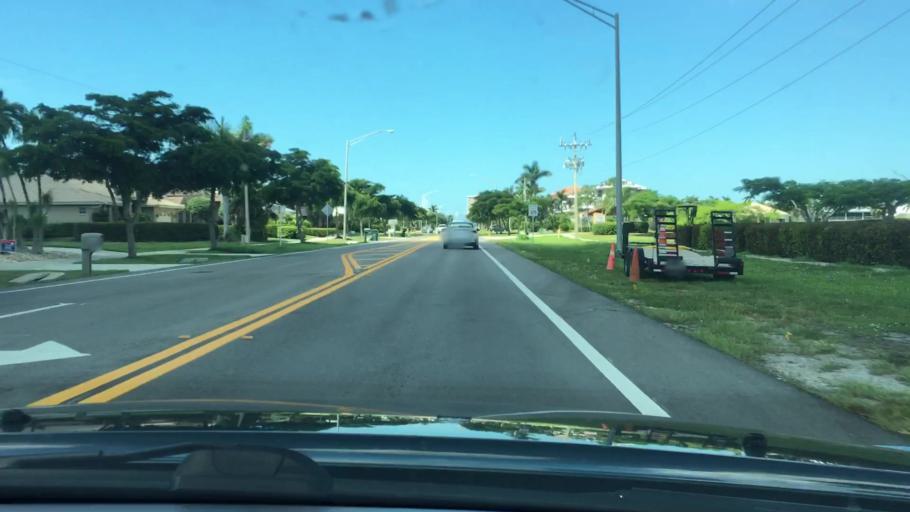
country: US
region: Florida
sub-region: Collier County
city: Marco
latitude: 25.9371
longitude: -81.7166
